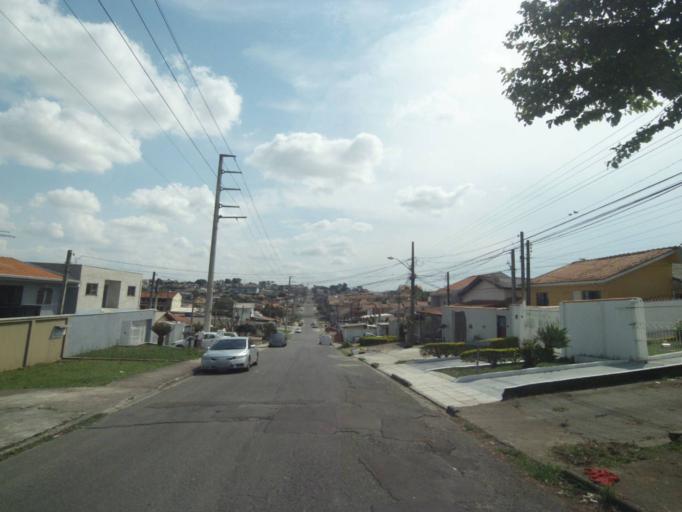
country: BR
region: Parana
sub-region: Pinhais
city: Pinhais
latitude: -25.4030
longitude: -49.2019
